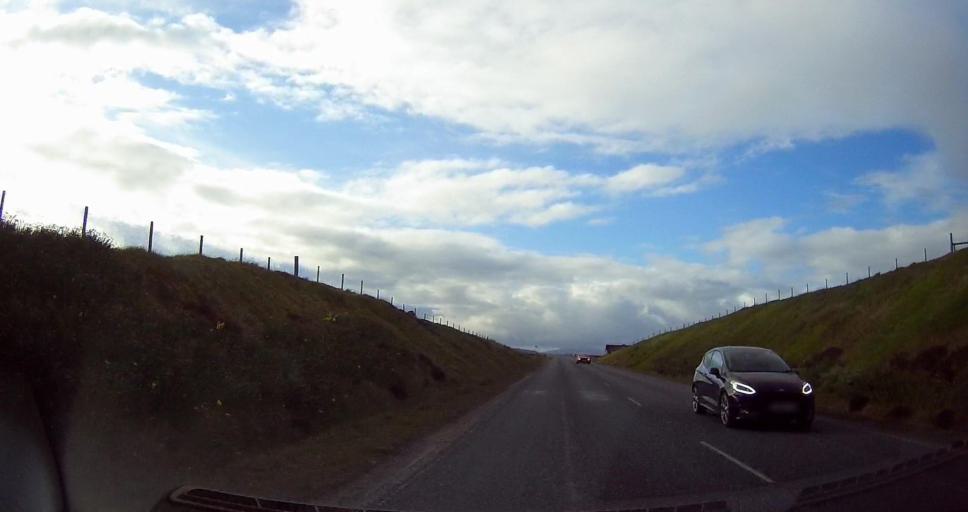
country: GB
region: Scotland
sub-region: Shetland Islands
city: Lerwick
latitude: 60.3754
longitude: -1.3383
